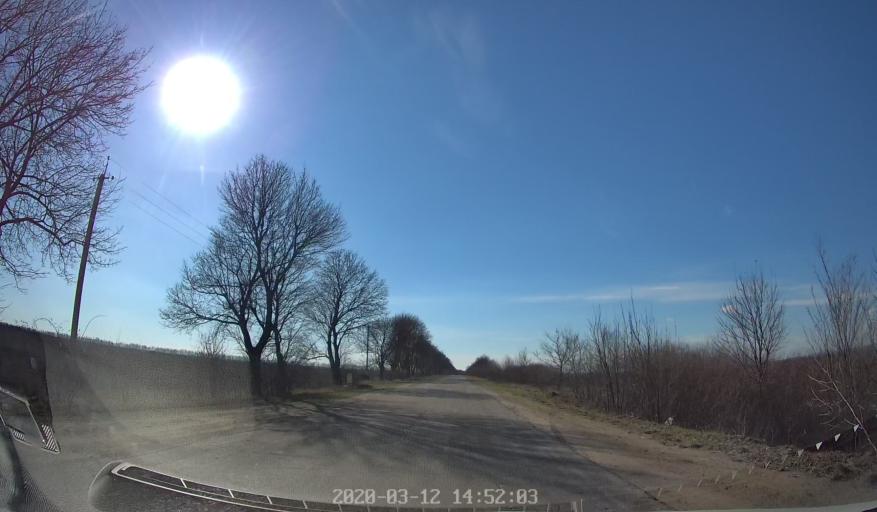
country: MD
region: Criuleni
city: Criuleni
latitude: 47.2209
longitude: 29.1057
